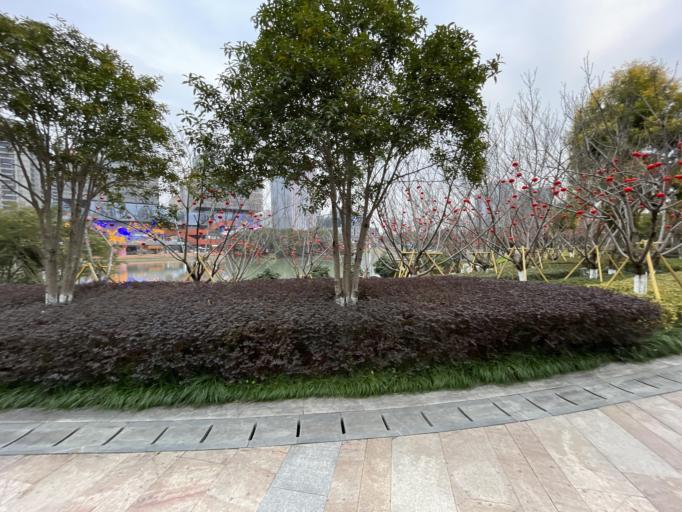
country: CN
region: Zhejiang Sheng
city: Wenzhou
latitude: 27.9863
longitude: 120.6947
